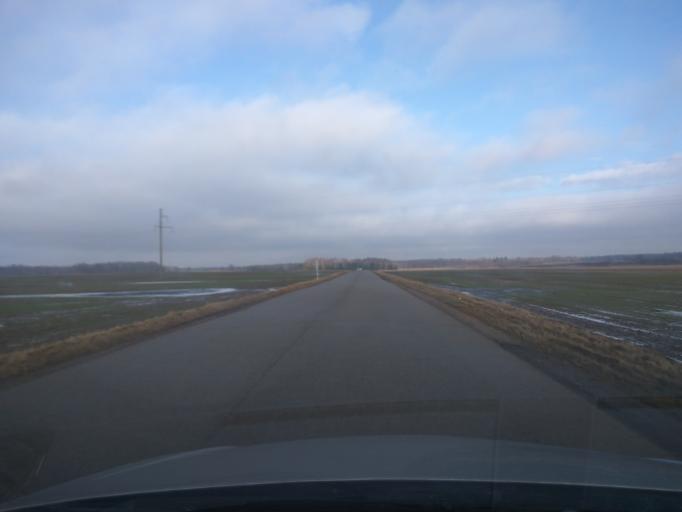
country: LV
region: Saldus Rajons
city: Saldus
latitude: 56.7483
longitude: 22.3850
